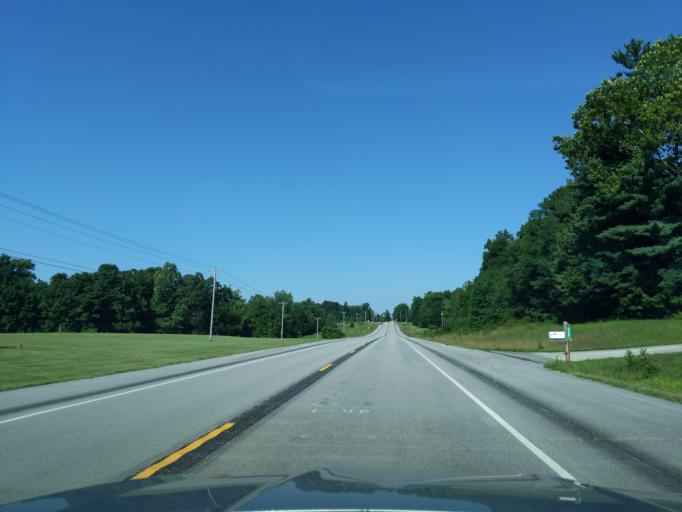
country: US
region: Indiana
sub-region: Ripley County
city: Osgood
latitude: 39.0750
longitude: -85.3217
